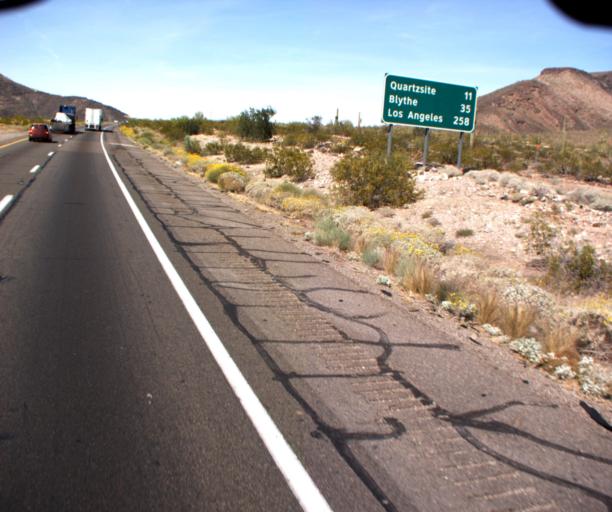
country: US
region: Arizona
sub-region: La Paz County
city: Quartzsite
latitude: 33.6645
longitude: -114.0301
